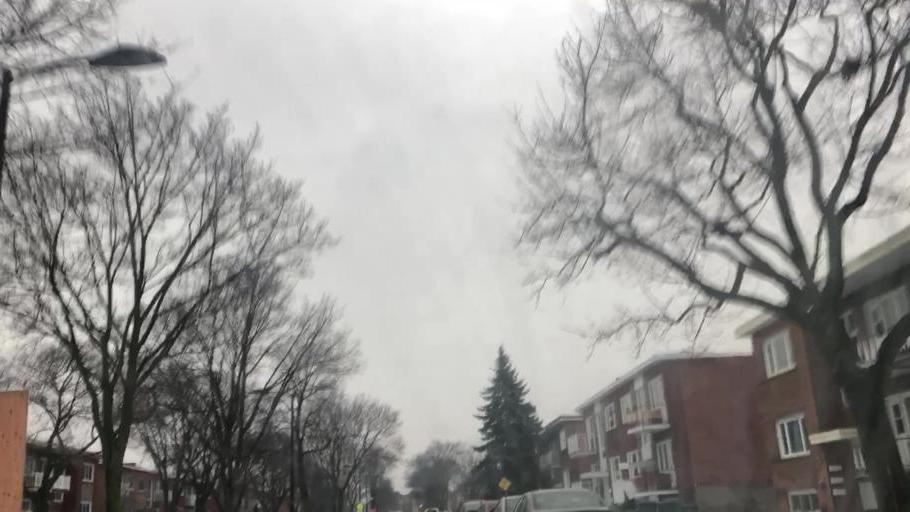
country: CA
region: Quebec
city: Saint-Laurent
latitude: 45.5158
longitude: -73.7235
